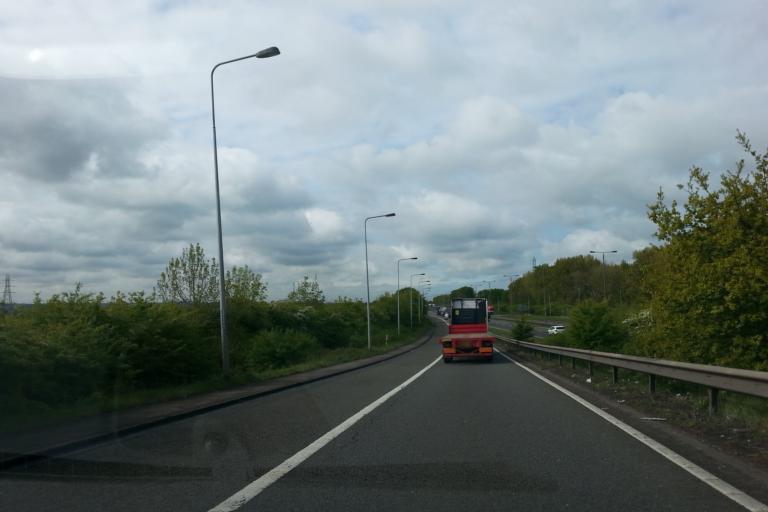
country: GB
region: England
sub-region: Derbyshire
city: Findern
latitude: 52.8640
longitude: -1.5700
